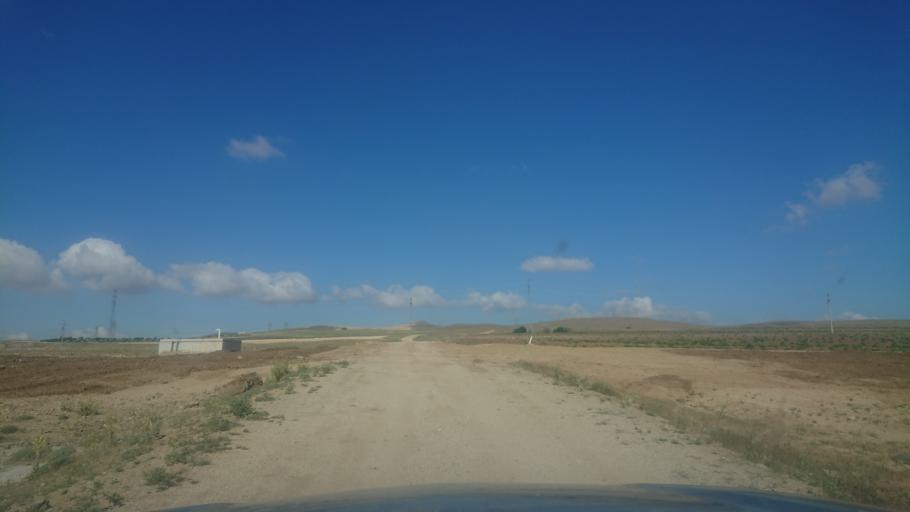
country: TR
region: Aksaray
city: Agacoren
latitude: 38.9182
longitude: 33.9206
